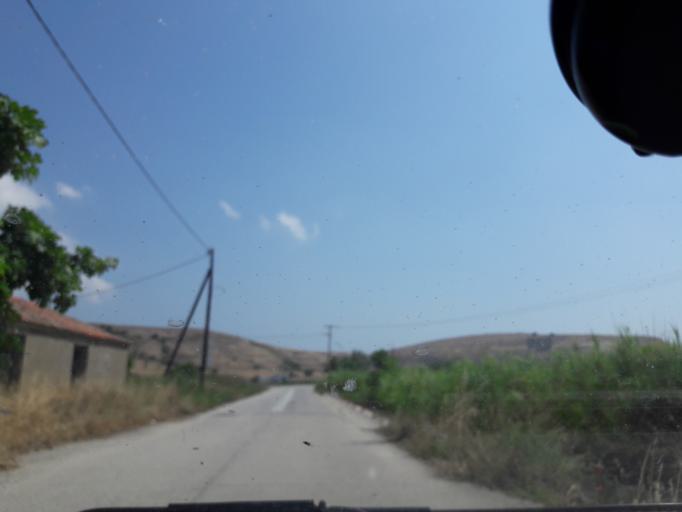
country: GR
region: North Aegean
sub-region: Nomos Lesvou
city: Myrina
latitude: 39.8702
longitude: 25.2699
